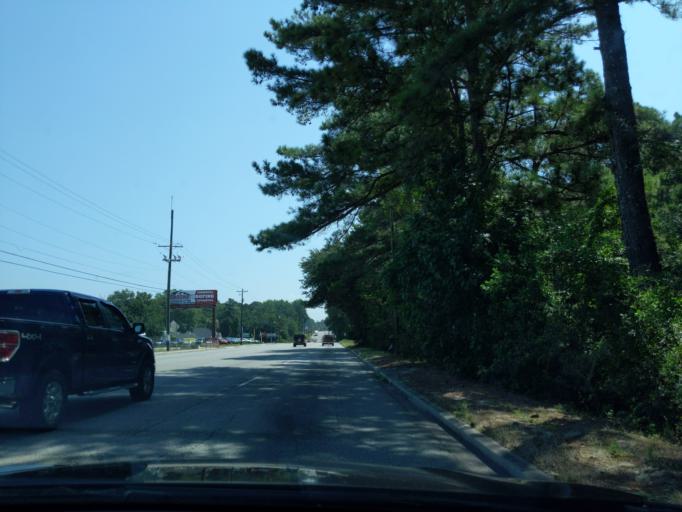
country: US
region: South Carolina
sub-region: Lexington County
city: Oak Grove
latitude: 33.9738
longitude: -81.1332
